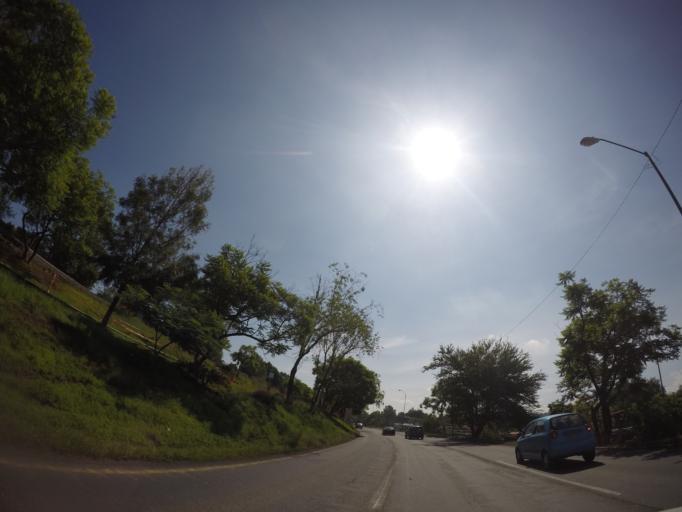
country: MX
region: Michoacan
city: Morelia
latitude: 19.7191
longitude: -101.1820
